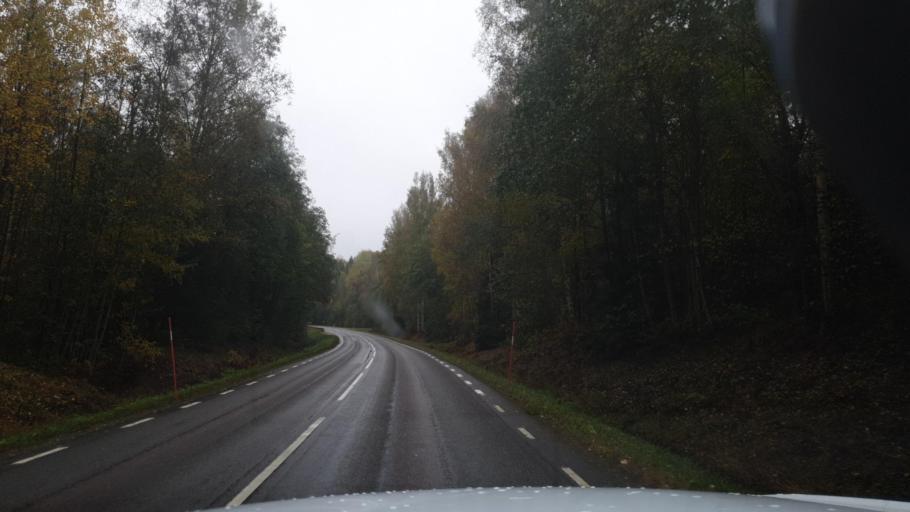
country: SE
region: Vaermland
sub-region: Eda Kommun
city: Amotfors
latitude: 59.6916
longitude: 12.3454
